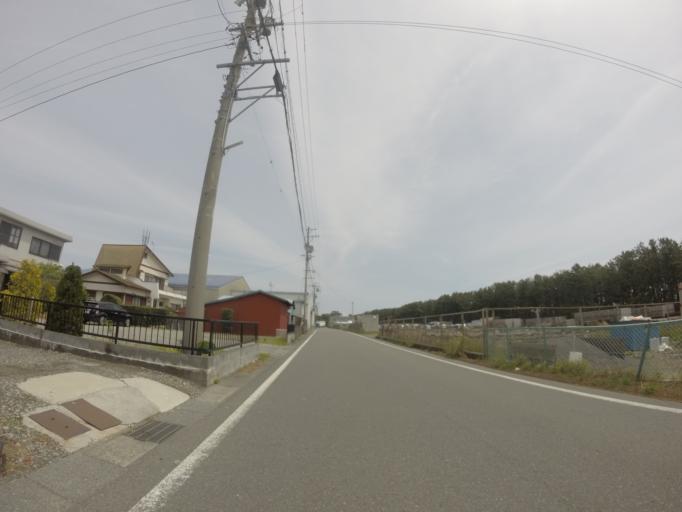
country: JP
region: Shizuoka
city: Yaizu
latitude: 34.8029
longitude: 138.3146
